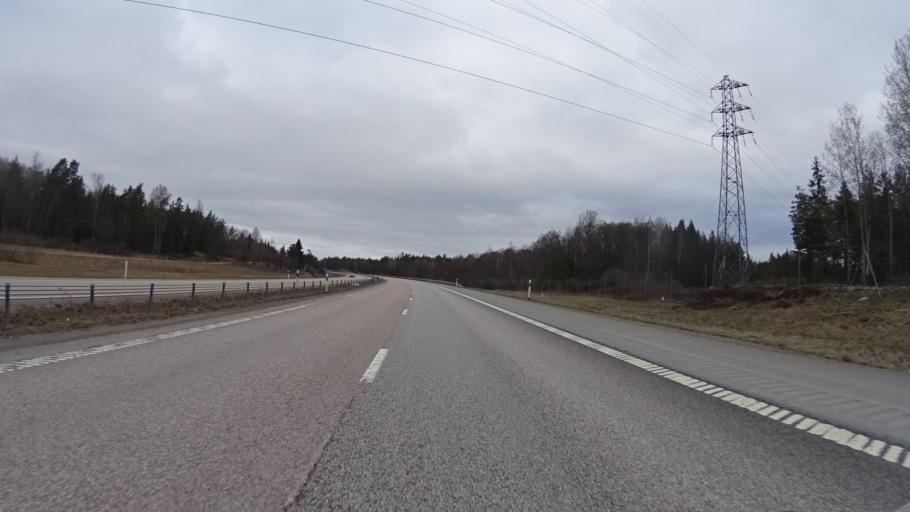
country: SE
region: Soedermanland
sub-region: Strangnas Kommun
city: Strangnas
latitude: 59.3569
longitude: 16.9997
